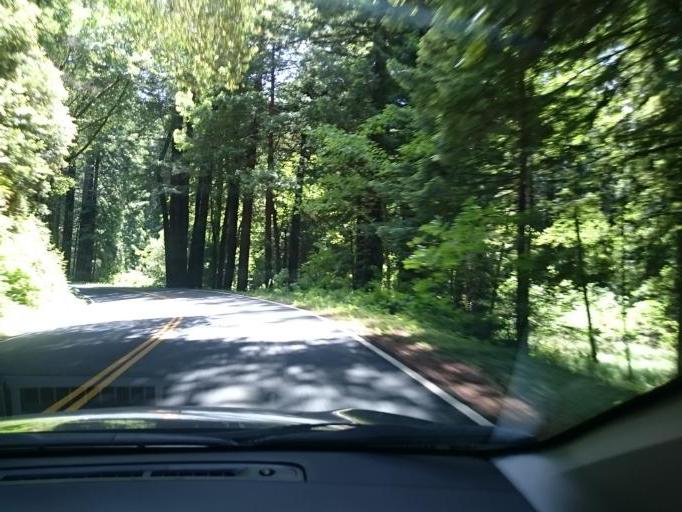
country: US
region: California
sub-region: Mendocino County
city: Fort Bragg
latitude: 39.1780
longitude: -123.6923
